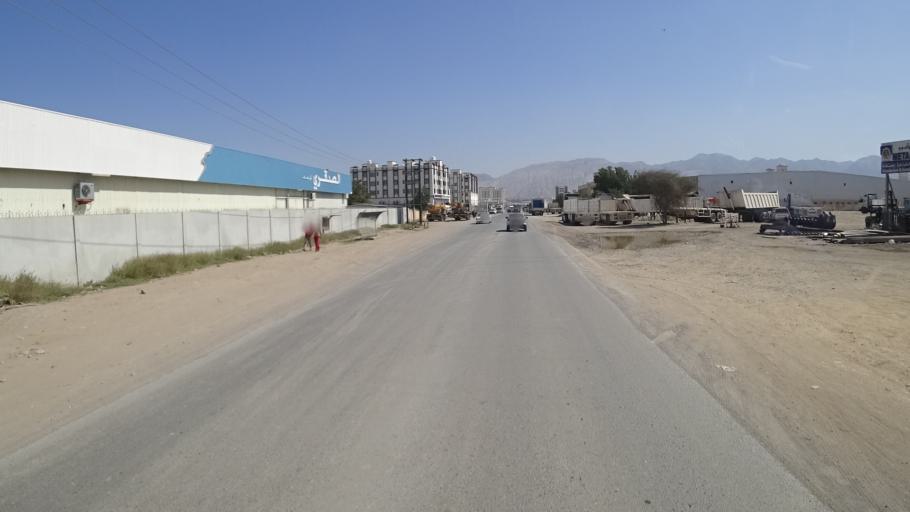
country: OM
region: Muhafazat Masqat
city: Bawshar
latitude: 23.5760
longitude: 58.3679
